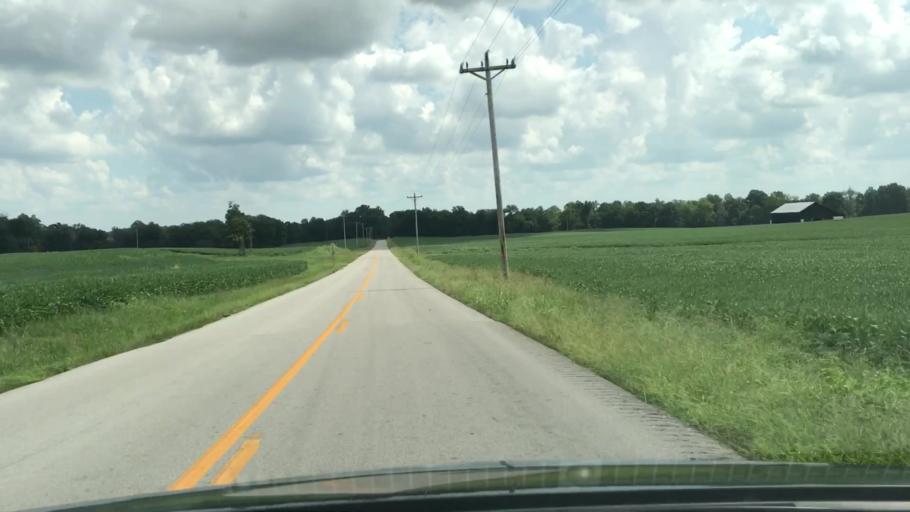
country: US
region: Kentucky
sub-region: Todd County
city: Elkton
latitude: 36.7927
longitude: -87.1479
